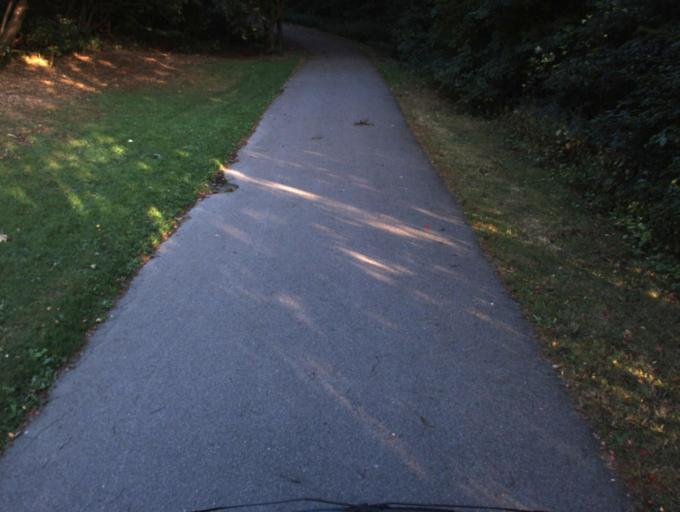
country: SE
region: Skane
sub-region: Helsingborg
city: Helsingborg
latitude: 56.0281
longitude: 12.7240
